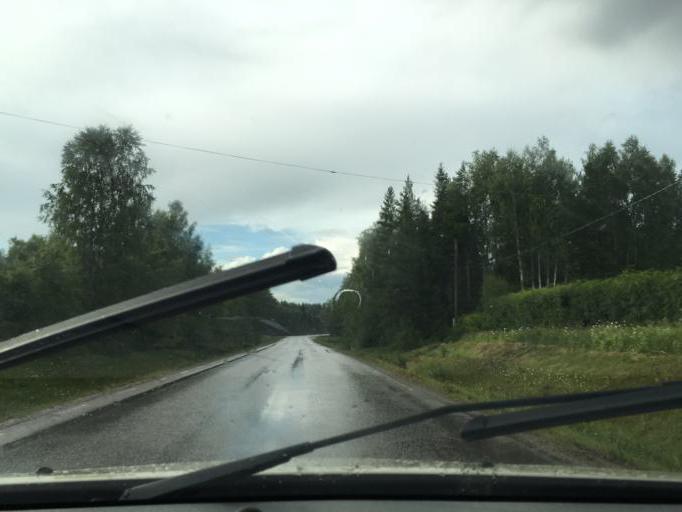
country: SE
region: Norrbotten
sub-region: Kalix Kommun
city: Rolfs
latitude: 65.9429
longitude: 22.8923
